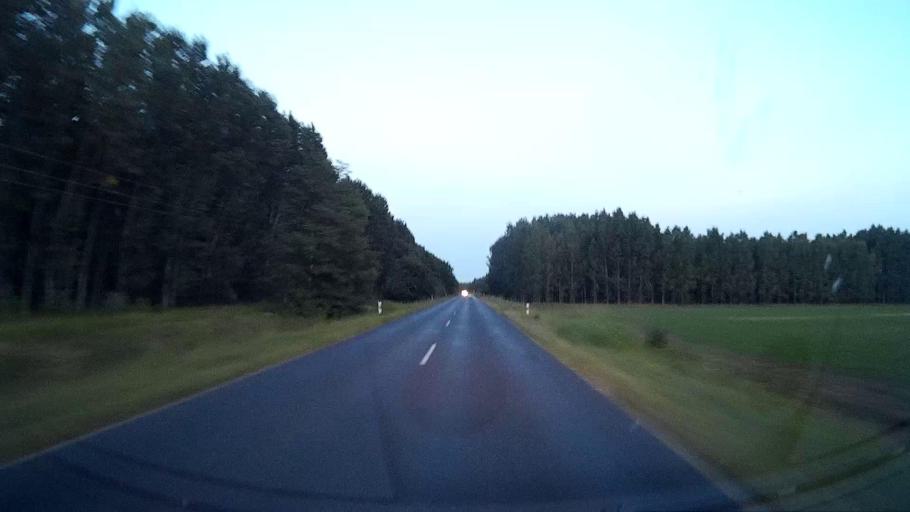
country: HU
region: Pest
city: Cegledbercel
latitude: 47.1996
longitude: 19.7070
